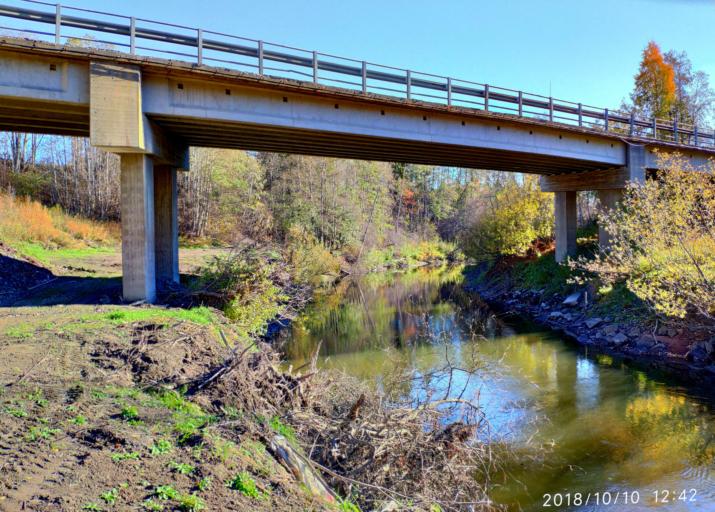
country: NO
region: Akershus
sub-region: Nannestad
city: Teigebyen
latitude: 60.1716
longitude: 11.0299
